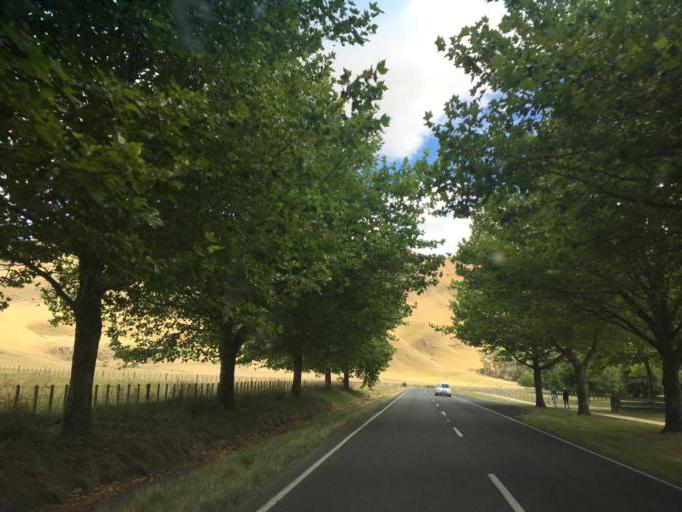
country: NZ
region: Hawke's Bay
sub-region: Hastings District
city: Hastings
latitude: -39.6957
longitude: 176.9225
